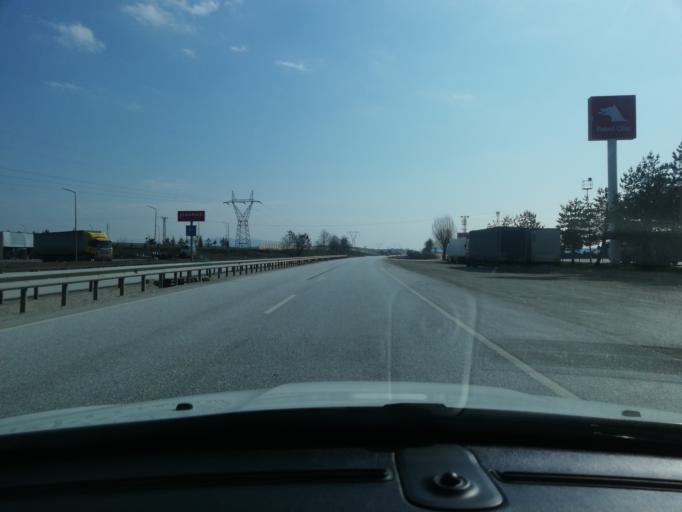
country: TR
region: Cankiri
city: Kursunlu
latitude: 40.8414
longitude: 33.1669
